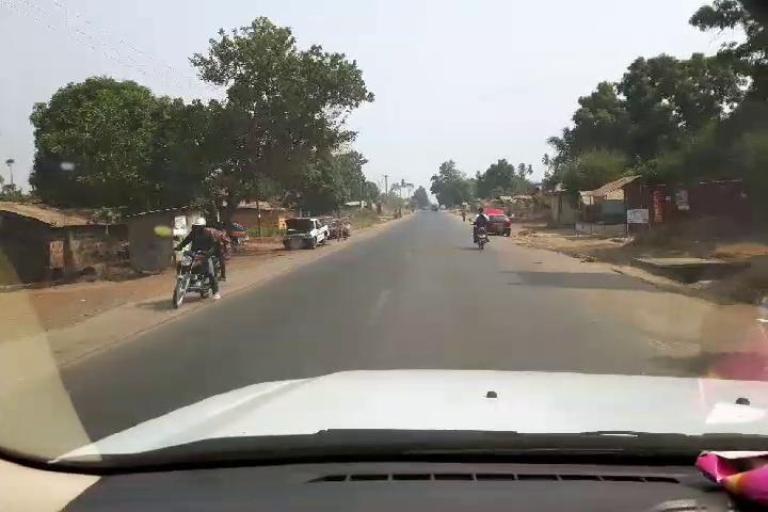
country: SL
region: Western Area
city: Waterloo
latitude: 8.3110
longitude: -13.0757
